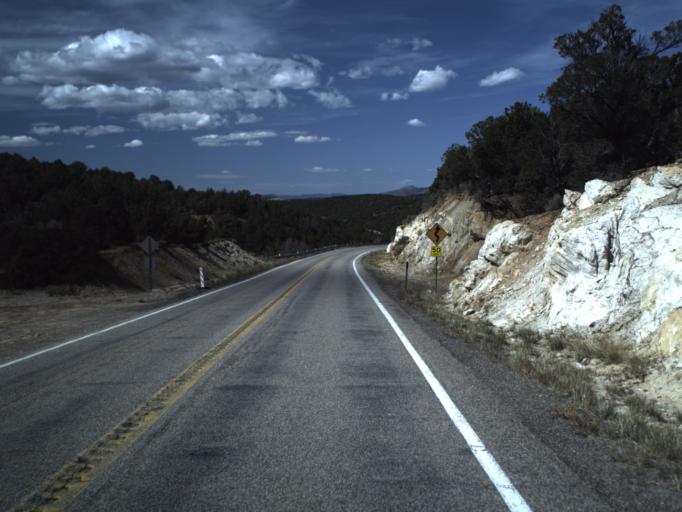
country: US
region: Utah
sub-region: Washington County
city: Enterprise
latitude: 37.5323
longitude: -113.6497
